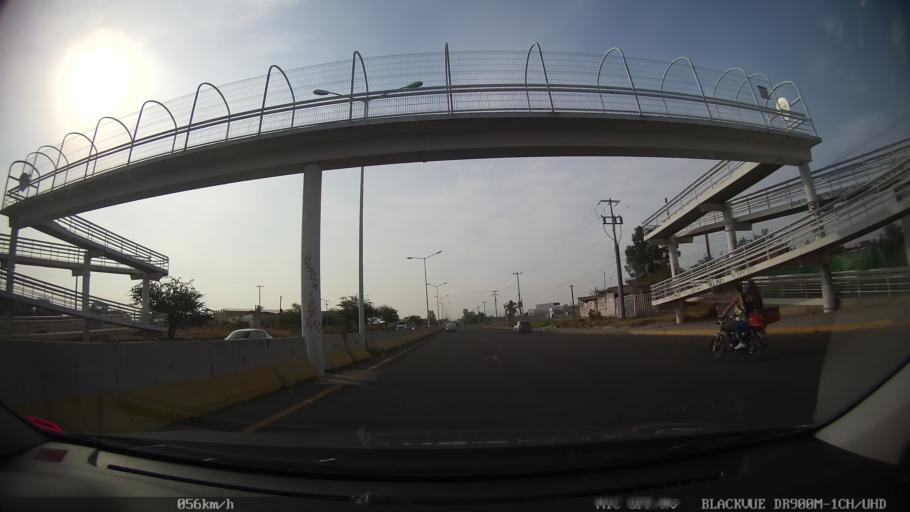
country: MX
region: Jalisco
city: Tonala
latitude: 20.6752
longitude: -103.2312
